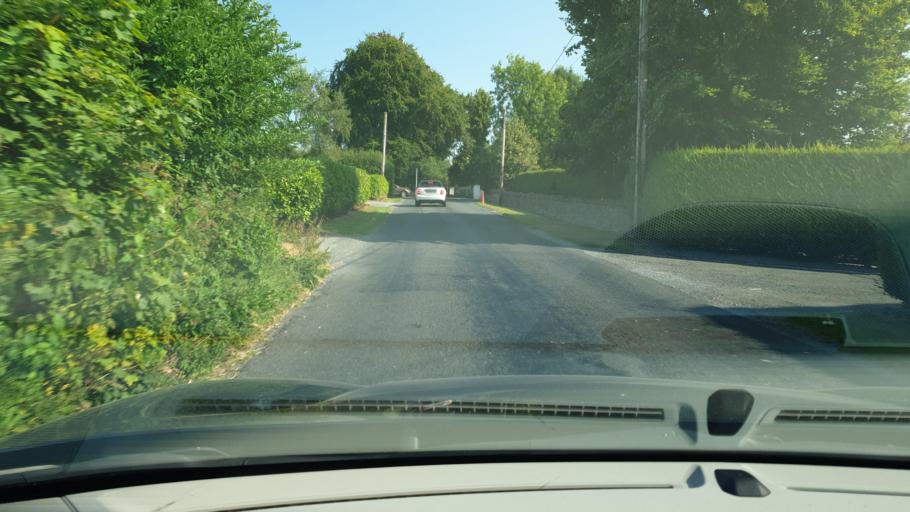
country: IE
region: Leinster
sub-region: An Mhi
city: Athboy
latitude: 53.6268
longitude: -6.9504
